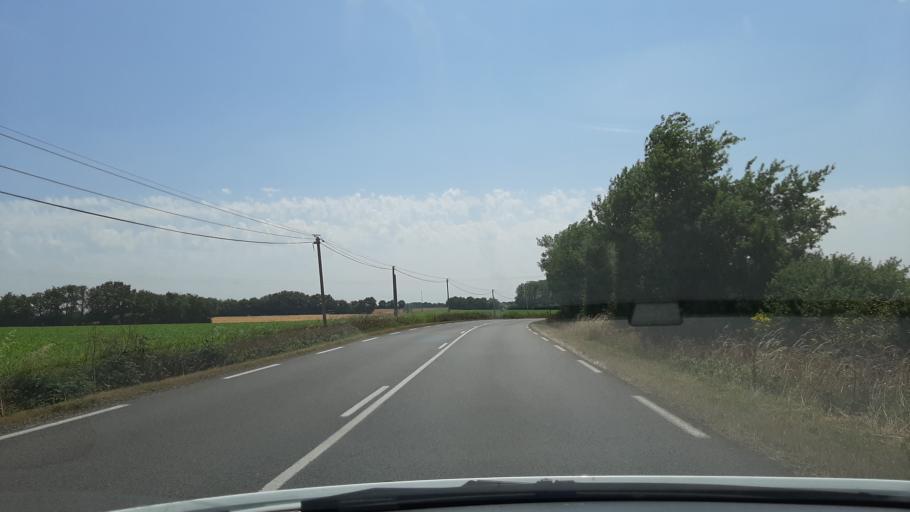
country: FR
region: Pays de la Loire
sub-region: Departement de la Vendee
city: Le Poire-sur-Vie
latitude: 46.7598
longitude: -1.4796
